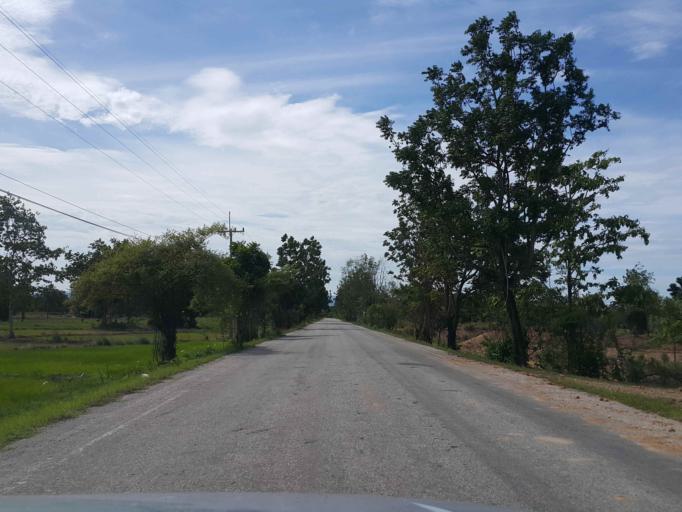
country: TH
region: Sukhothai
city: Ban Dan Lan Hoi
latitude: 17.1280
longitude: 99.5294
